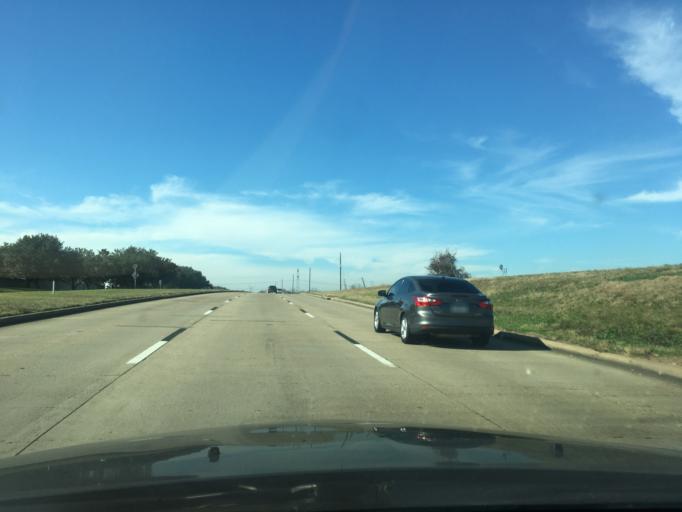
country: US
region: Texas
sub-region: Fort Bend County
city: New Territory
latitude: 29.6015
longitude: -95.6861
